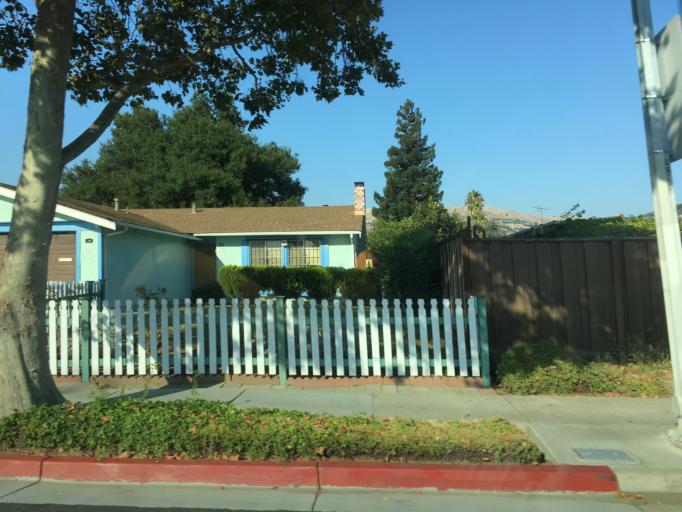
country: US
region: California
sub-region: Santa Clara County
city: Alum Rock
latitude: 37.3710
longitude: -121.8323
